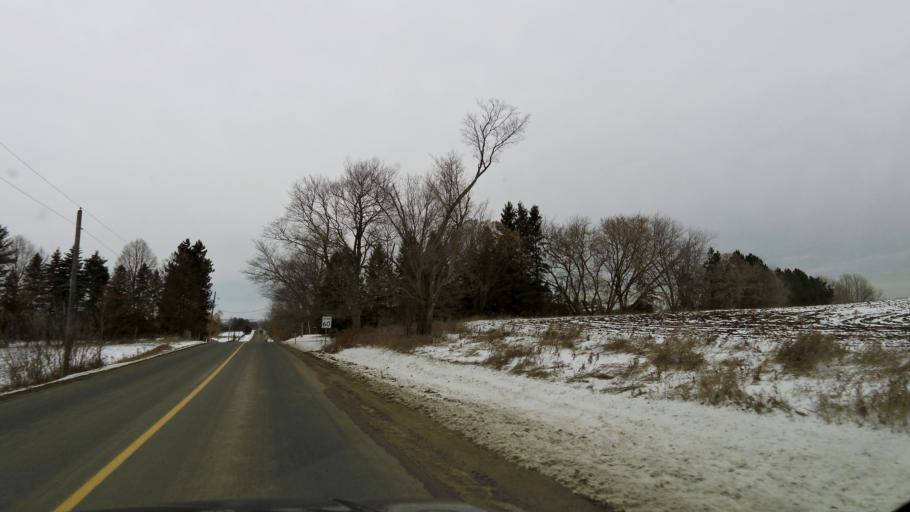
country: CA
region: Ontario
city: Bradford West Gwillimbury
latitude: 43.9684
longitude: -79.6429
